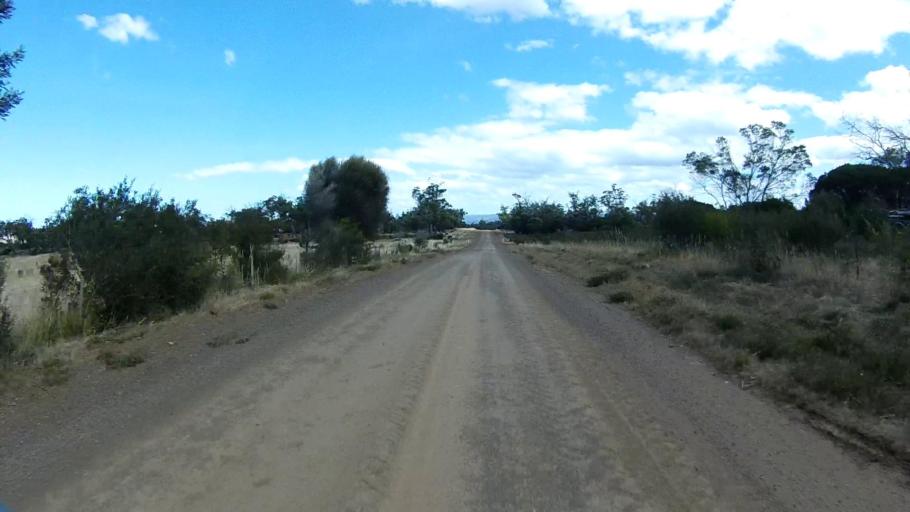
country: AU
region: Tasmania
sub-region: Break O'Day
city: St Helens
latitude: -41.9785
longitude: 148.0688
